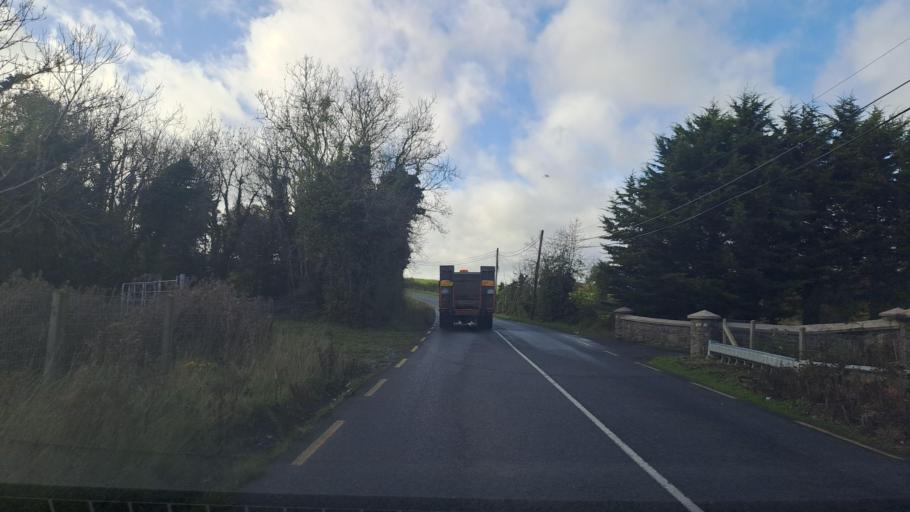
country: IE
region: Ulster
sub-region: County Monaghan
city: Monaghan
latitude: 54.1188
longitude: -6.9212
